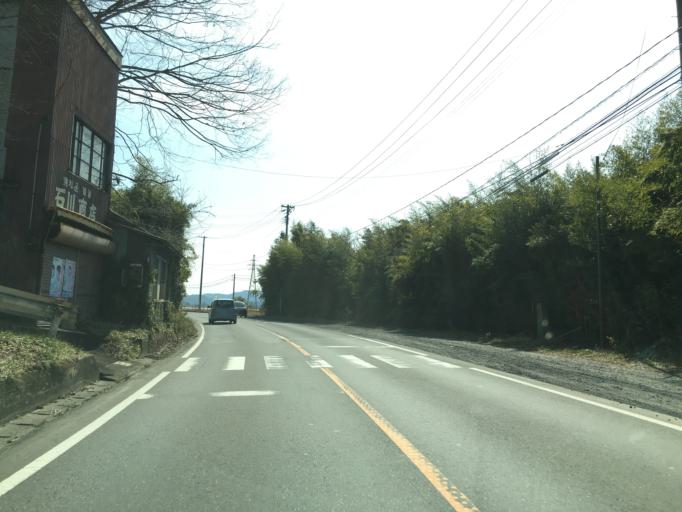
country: JP
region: Ibaraki
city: Daigo
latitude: 36.9256
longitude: 140.4148
